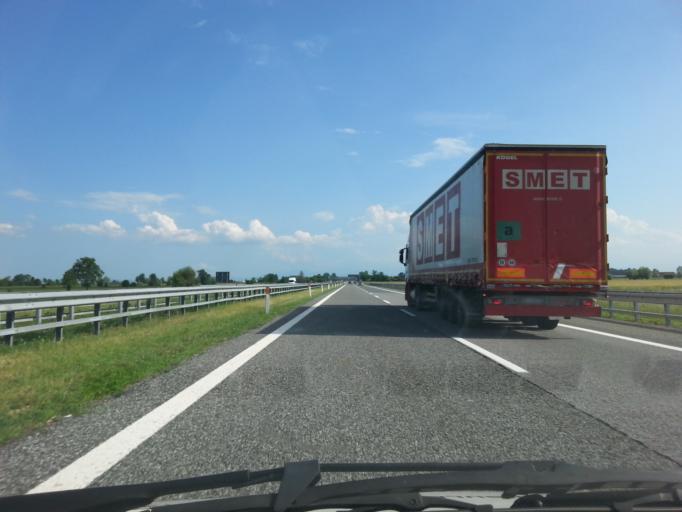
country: IT
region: Piedmont
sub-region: Provincia di Cuneo
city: Marene
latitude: 44.6864
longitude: 7.7680
